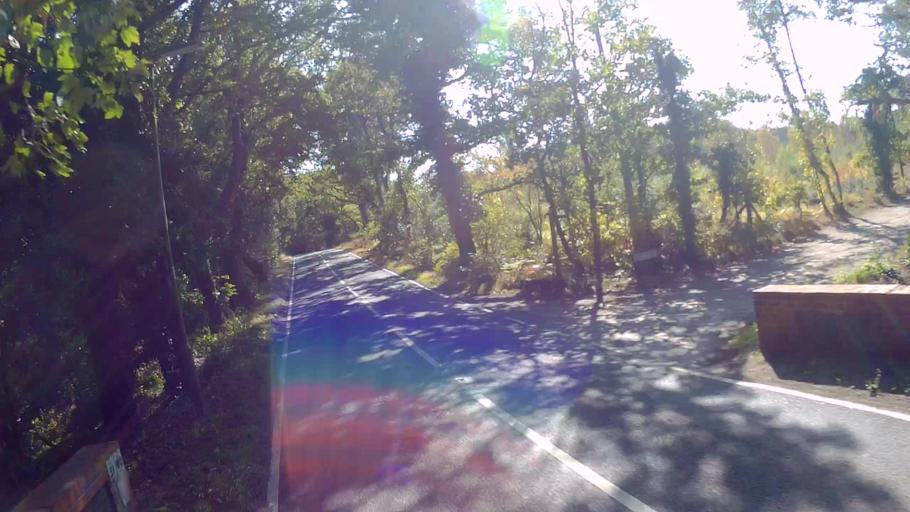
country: GB
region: England
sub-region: Surrey
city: Farnham
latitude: 51.1976
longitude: -0.7728
